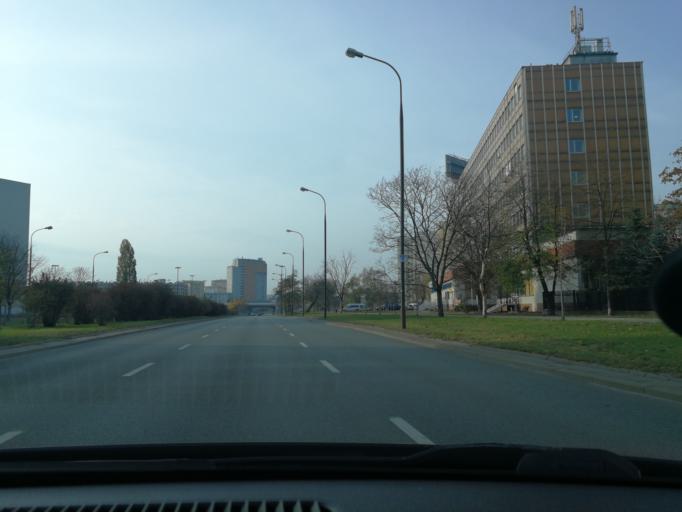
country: PL
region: Masovian Voivodeship
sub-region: Warszawa
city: Praga Poludnie
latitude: 52.2379
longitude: 21.0801
